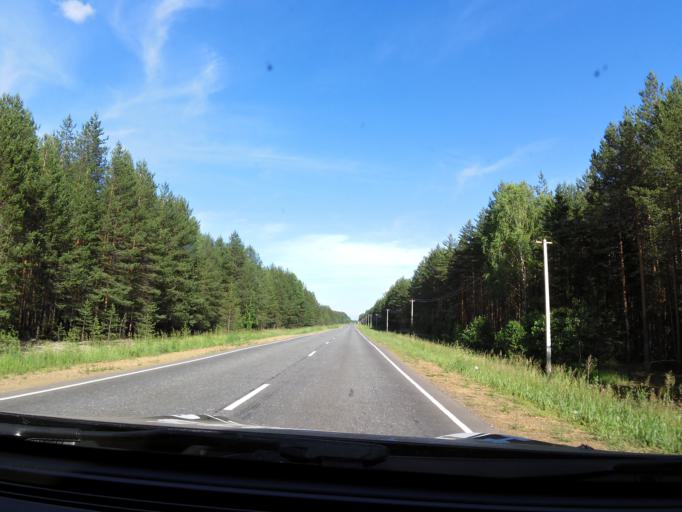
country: RU
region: Kirov
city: Belaya Kholunitsa
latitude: 58.9077
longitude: 51.0005
